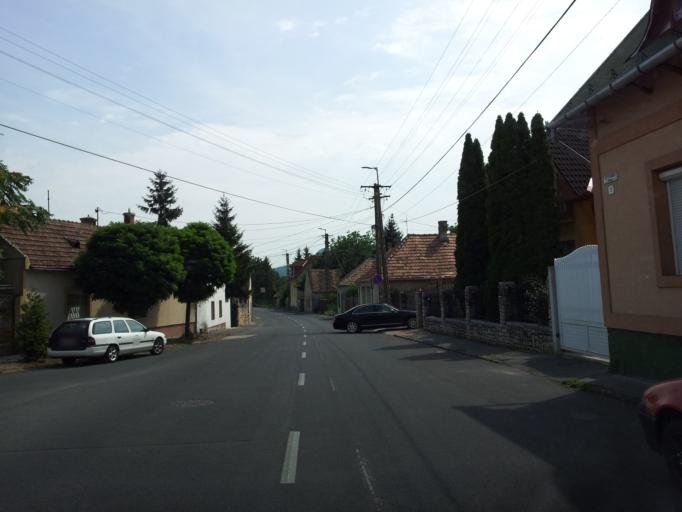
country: HU
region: Veszprem
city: Tapolca
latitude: 46.8796
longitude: 17.4433
